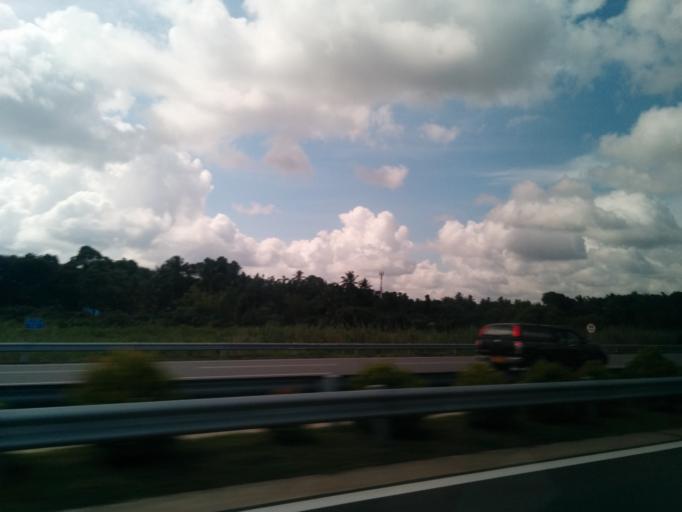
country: LK
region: Western
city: Hendala
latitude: 6.9962
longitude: 79.9041
